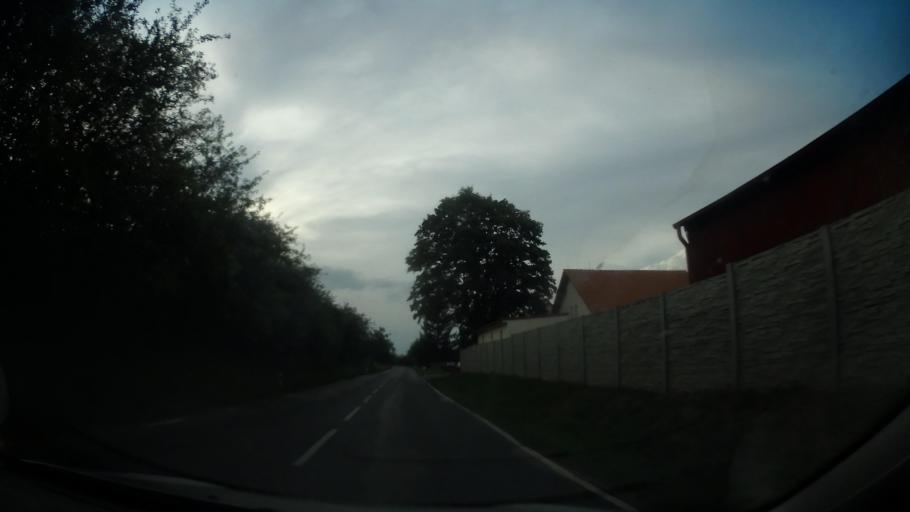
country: CZ
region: Central Bohemia
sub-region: Okres Kutna Hora
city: Caslav
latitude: 49.9020
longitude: 15.4156
